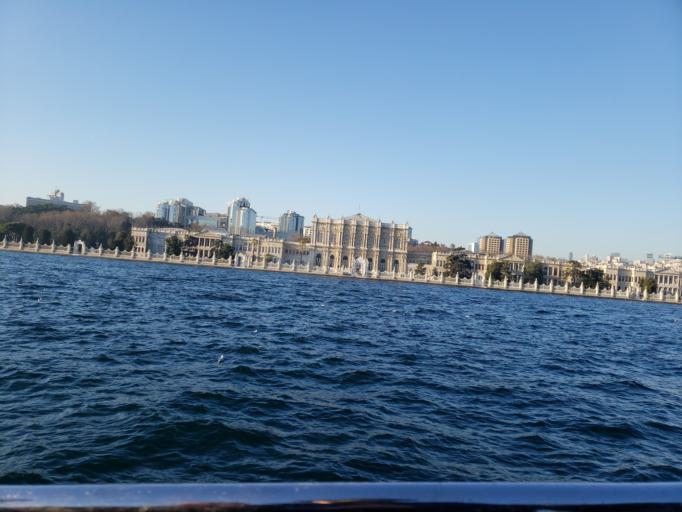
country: TR
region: Istanbul
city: UEskuedar
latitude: 41.0361
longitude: 29.0018
